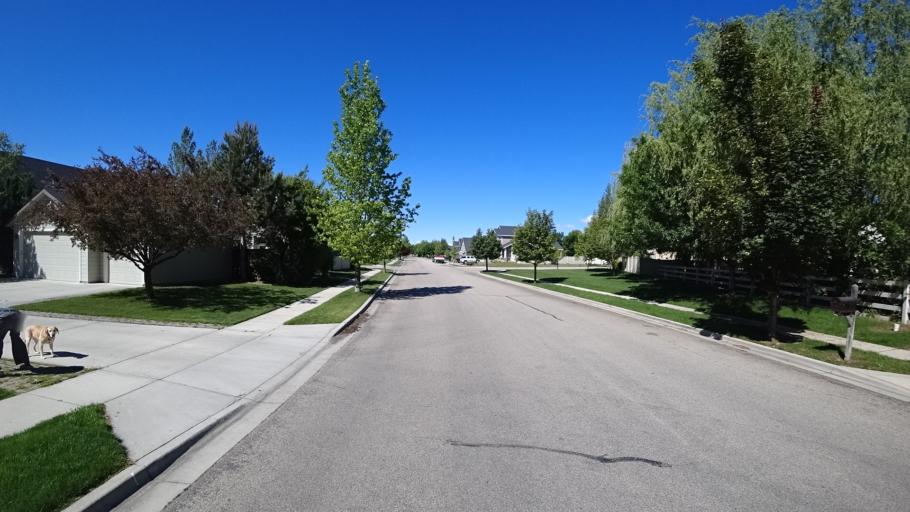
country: US
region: Idaho
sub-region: Ada County
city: Meridian
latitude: 43.6410
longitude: -116.3781
